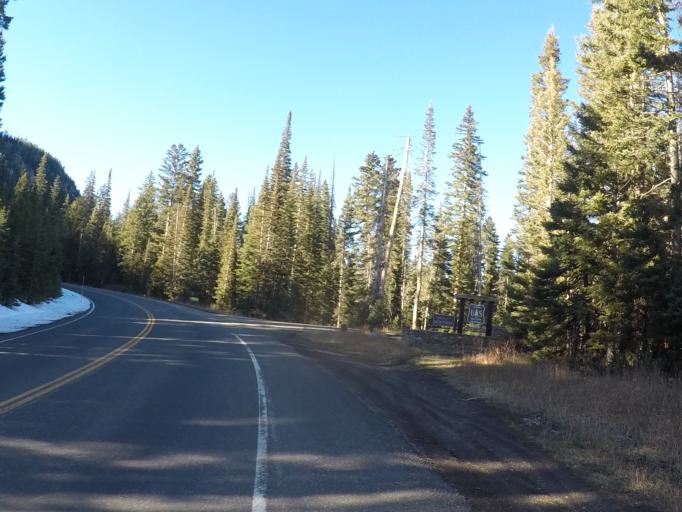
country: US
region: Montana
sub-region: Carbon County
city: Red Lodge
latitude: 45.0017
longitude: -109.8557
